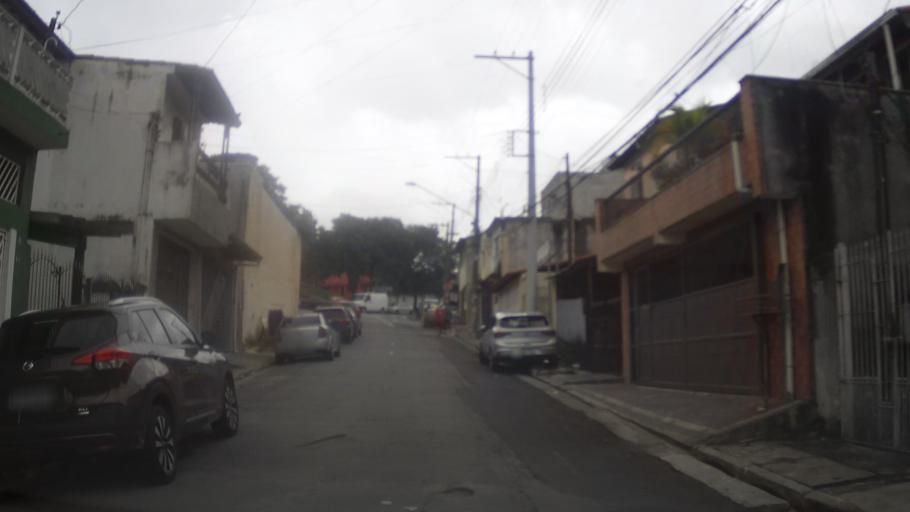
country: BR
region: Sao Paulo
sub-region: Guarulhos
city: Guarulhos
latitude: -23.4513
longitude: -46.5246
